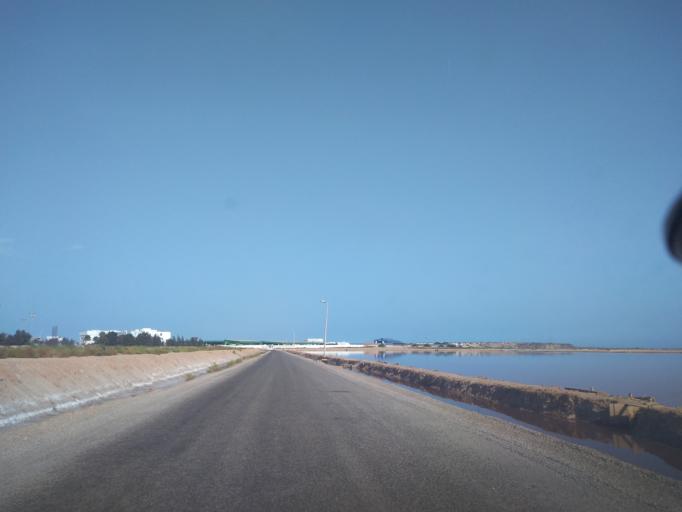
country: TN
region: Safaqis
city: Sfax
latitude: 34.7259
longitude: 10.7483
